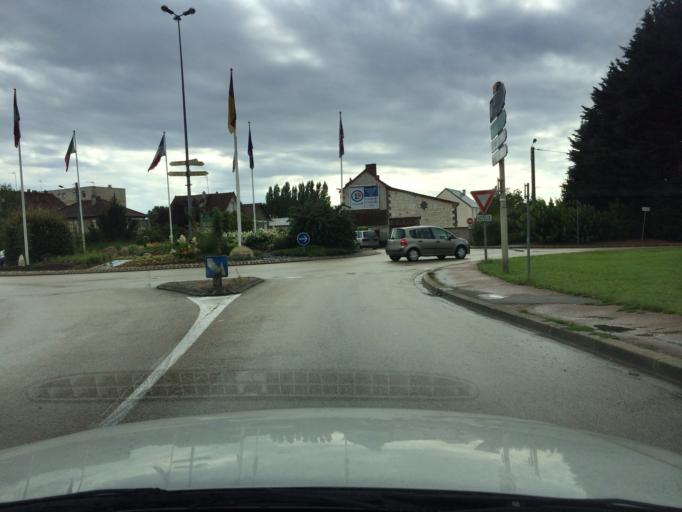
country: FR
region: Bourgogne
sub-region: Departement de l'Yonne
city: Joigny
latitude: 47.9779
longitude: 3.3866
